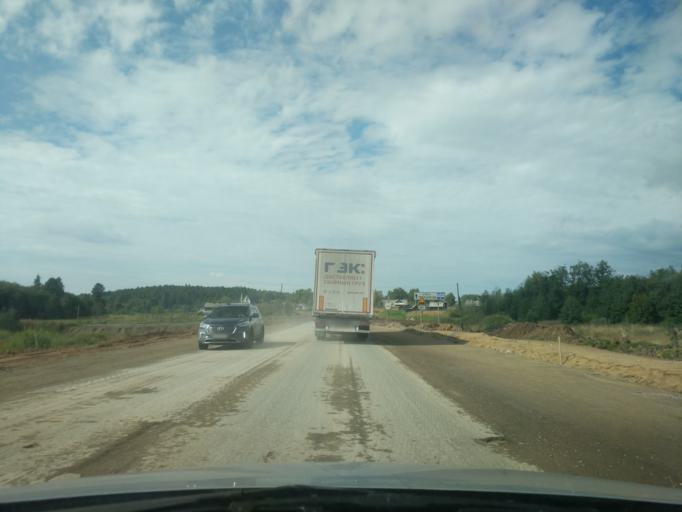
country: RU
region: Kostroma
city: Sudislavl'
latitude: 57.8755
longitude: 41.7330
